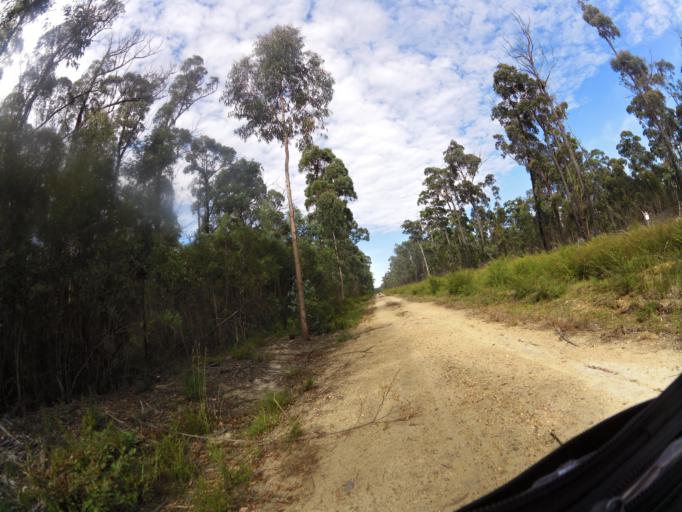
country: AU
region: Victoria
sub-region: East Gippsland
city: Lakes Entrance
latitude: -37.7458
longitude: 148.2393
